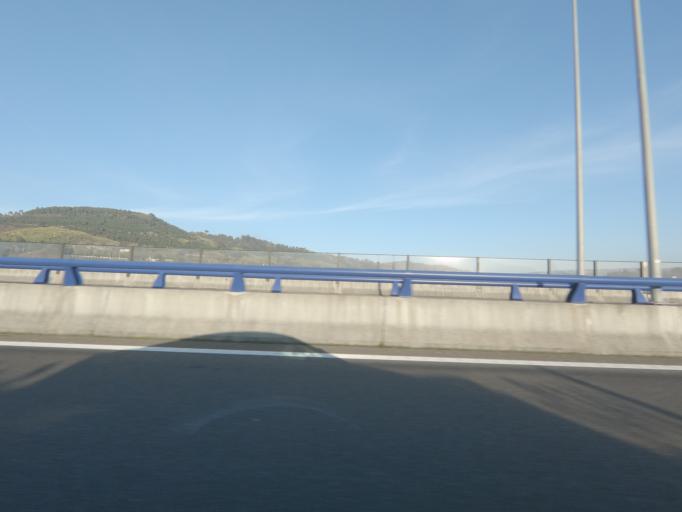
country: ES
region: Galicia
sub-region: Provincia de Ourense
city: Punxin
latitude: 42.3486
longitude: -7.9958
